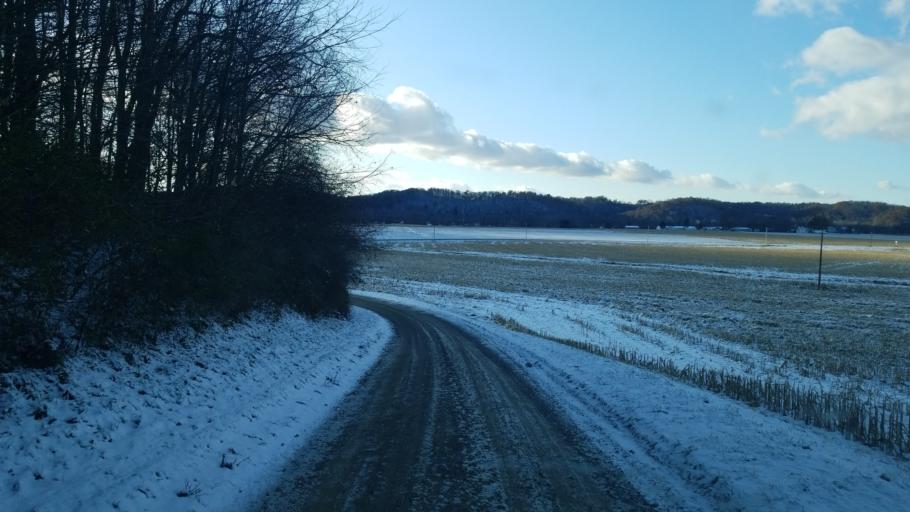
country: US
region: Ohio
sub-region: Licking County
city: Utica
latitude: 40.1674
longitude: -82.4045
